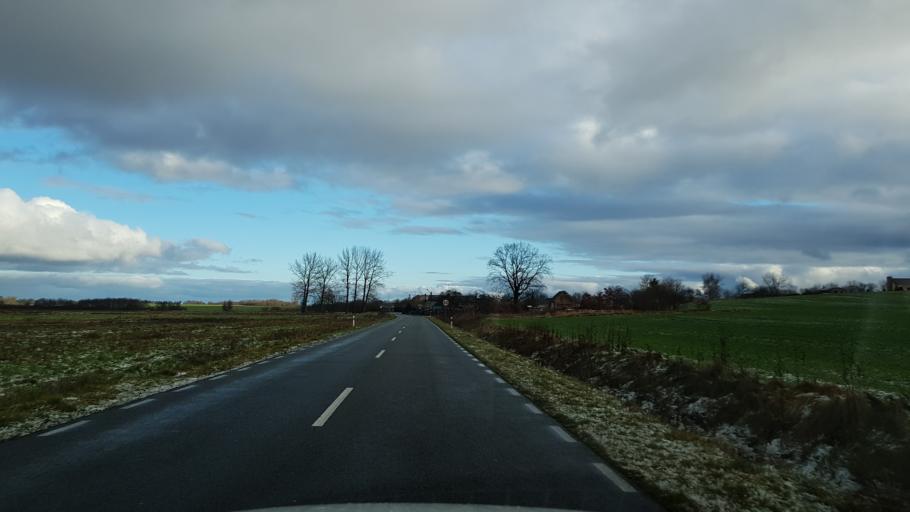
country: PL
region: West Pomeranian Voivodeship
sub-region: Powiat gryficki
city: Karnice
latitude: 54.0486
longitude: 15.0655
